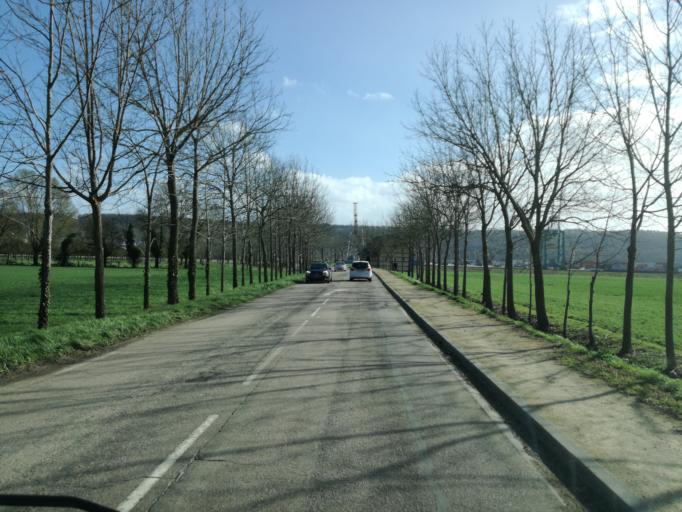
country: FR
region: Haute-Normandie
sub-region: Departement de la Seine-Maritime
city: Grand-Couronne
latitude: 49.3593
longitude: 0.9799
